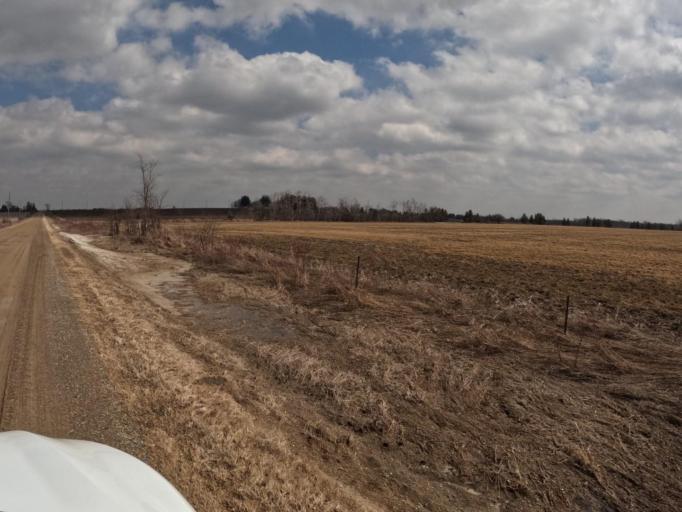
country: CA
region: Ontario
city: Shelburne
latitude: 44.0154
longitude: -80.3225
